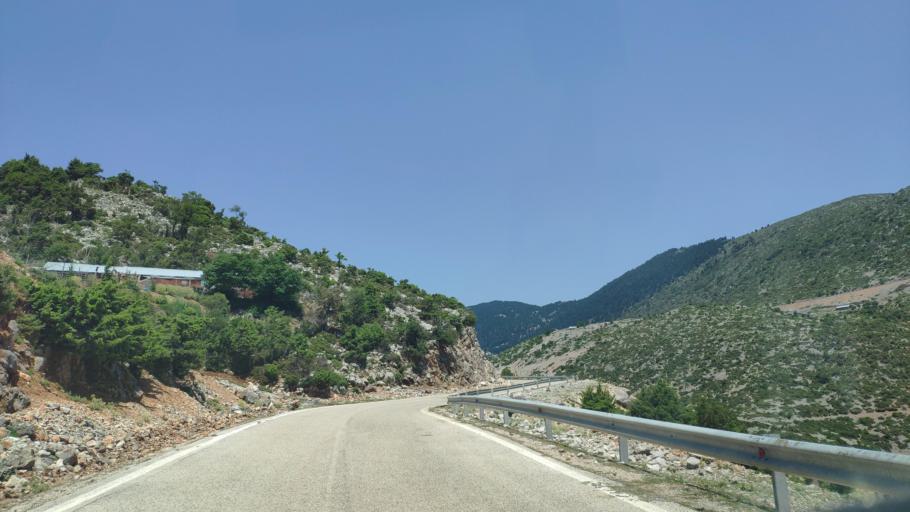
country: GR
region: West Greece
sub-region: Nomos Aitolias kai Akarnanias
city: Krikellos
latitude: 39.0421
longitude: 21.3758
